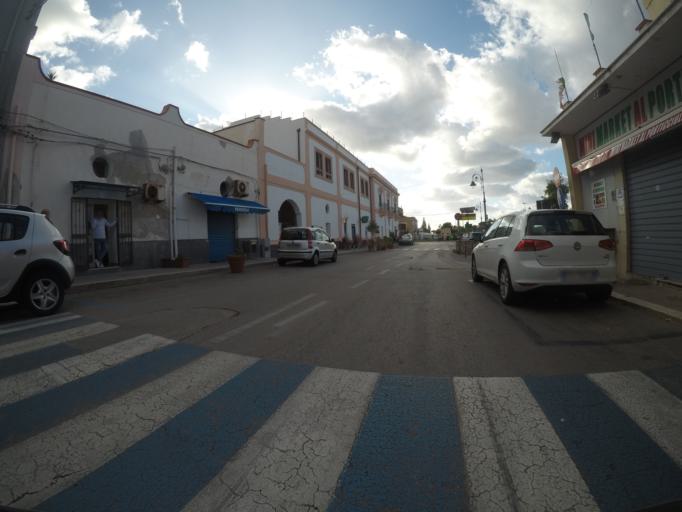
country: IT
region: Sicily
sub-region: Palermo
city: Isola delle Femmine
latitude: 38.1986
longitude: 13.2493
